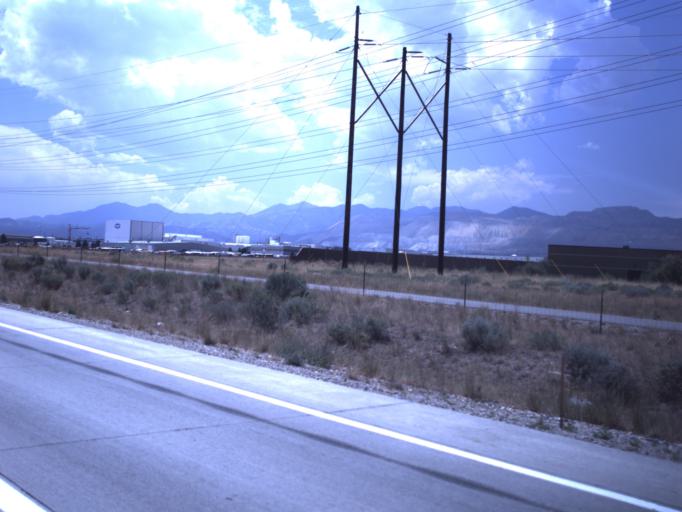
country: US
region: Utah
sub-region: Salt Lake County
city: Oquirrh
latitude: 40.5890
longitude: -112.0293
